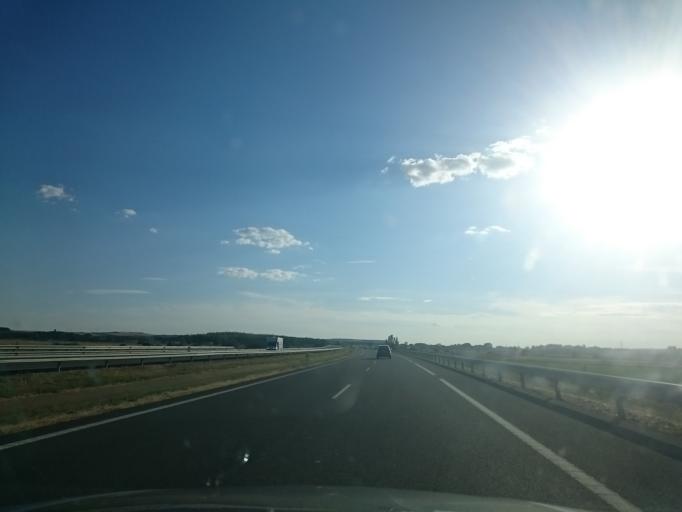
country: ES
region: Castille and Leon
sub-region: Provincia de Burgos
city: Melgar de Fernamental
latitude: 42.4118
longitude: -4.2572
